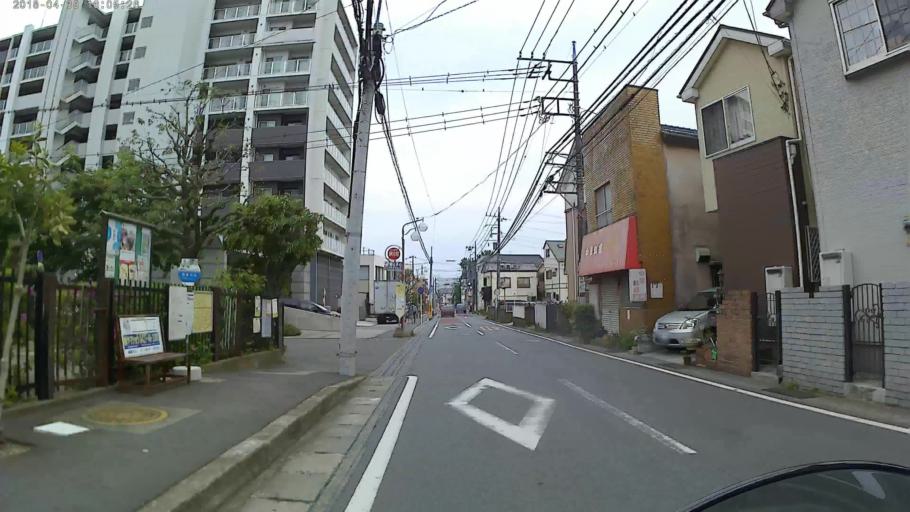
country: JP
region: Kanagawa
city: Minami-rinkan
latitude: 35.5048
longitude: 139.4267
